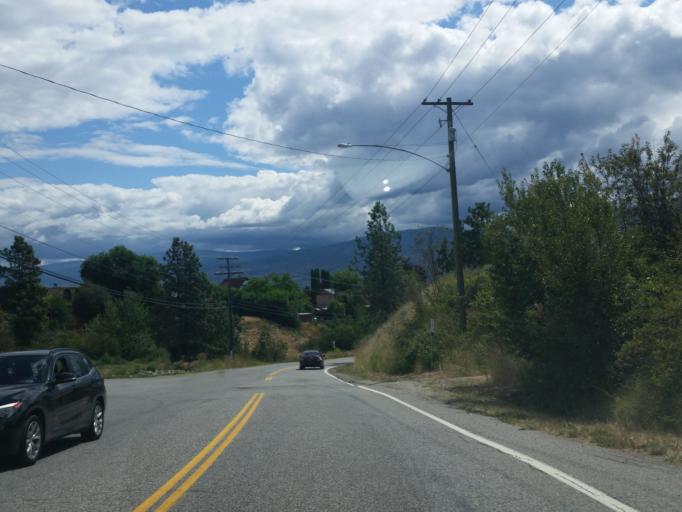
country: CA
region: British Columbia
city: West Kelowna
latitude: 49.8274
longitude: -119.6190
